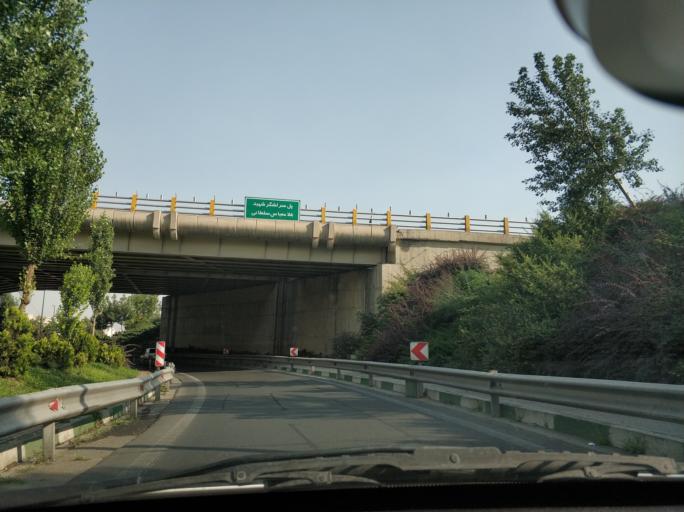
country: IR
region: Tehran
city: Tehran
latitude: 35.7400
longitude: 51.3680
